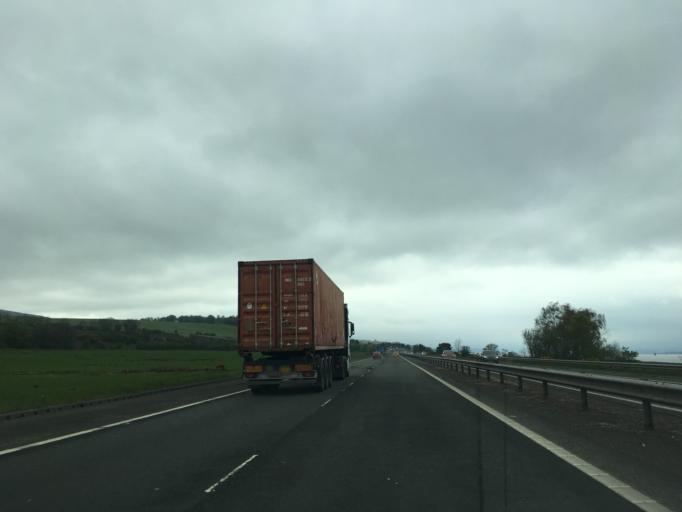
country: GB
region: Scotland
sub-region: Renfrewshire
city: Bishopton
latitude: 55.9229
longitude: -4.5388
